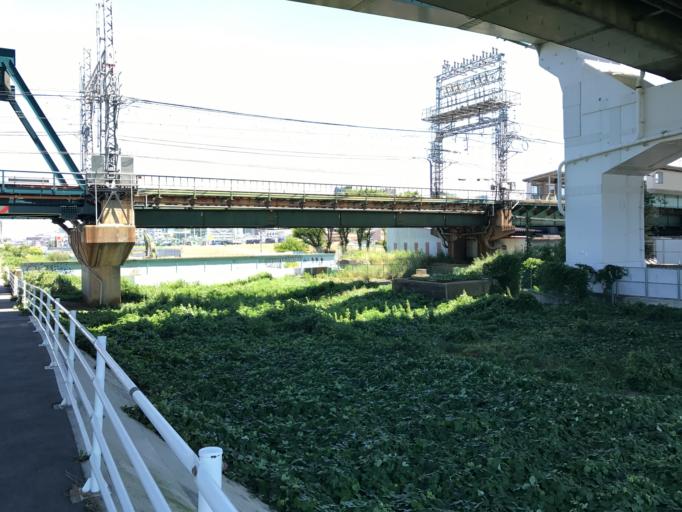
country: JP
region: Osaka
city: Osaka-shi
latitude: 34.6968
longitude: 135.4640
